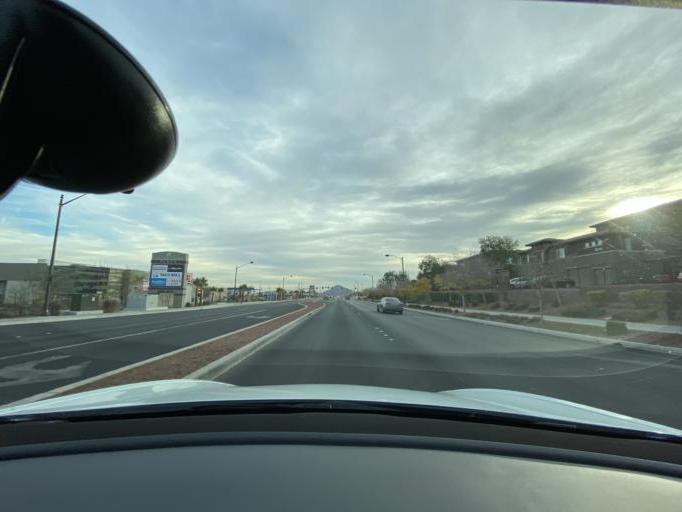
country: US
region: Nevada
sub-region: Clark County
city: Summerlin South
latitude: 36.2863
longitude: -115.3150
